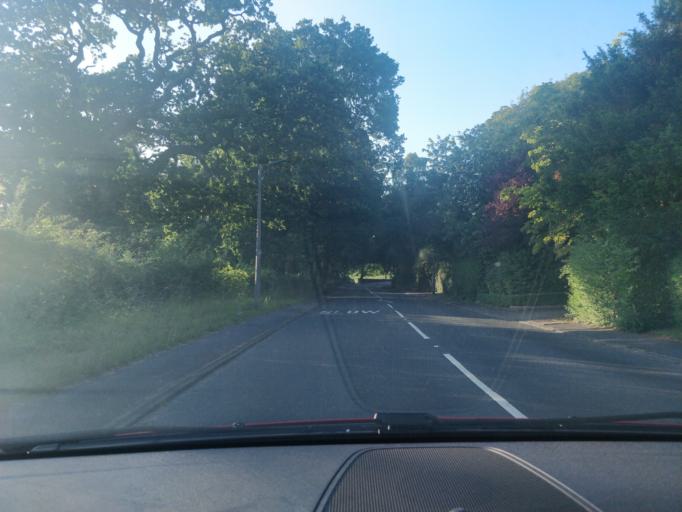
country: GB
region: England
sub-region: Lancashire
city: Parbold
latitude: 53.5984
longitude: -2.7684
